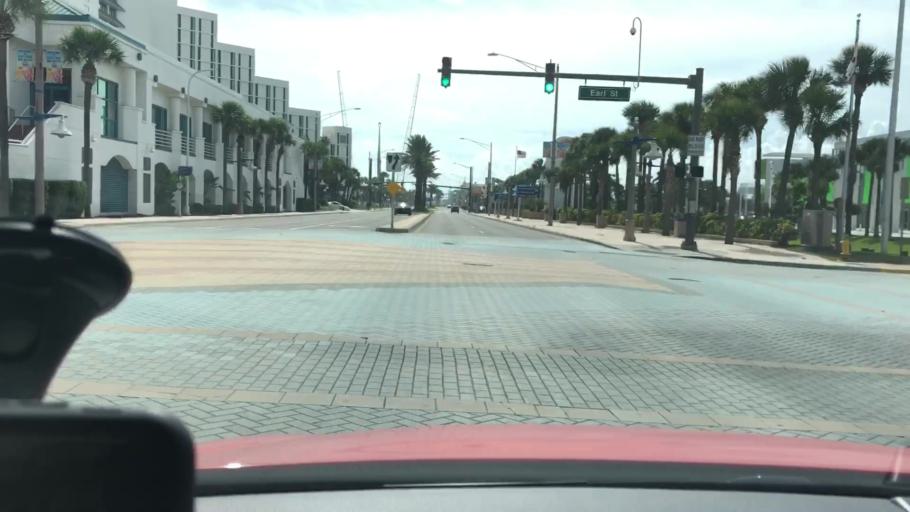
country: US
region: Florida
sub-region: Volusia County
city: Daytona Beach
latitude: 29.2300
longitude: -81.0098
